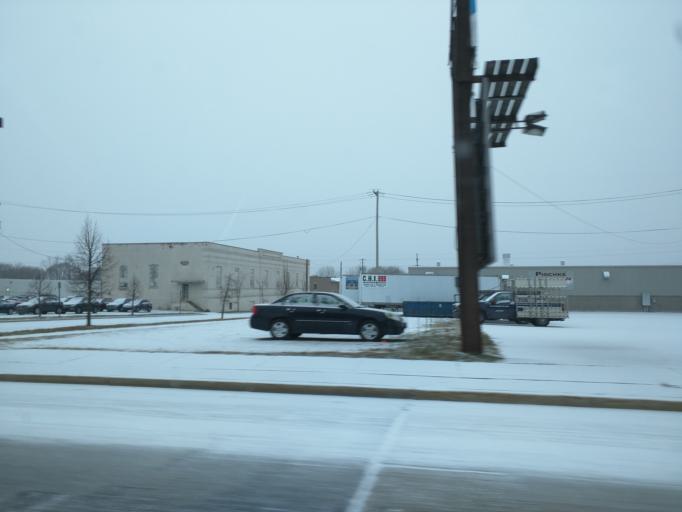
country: US
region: Wisconsin
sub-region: La Crosse County
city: La Crosse
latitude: 43.8070
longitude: -91.2536
